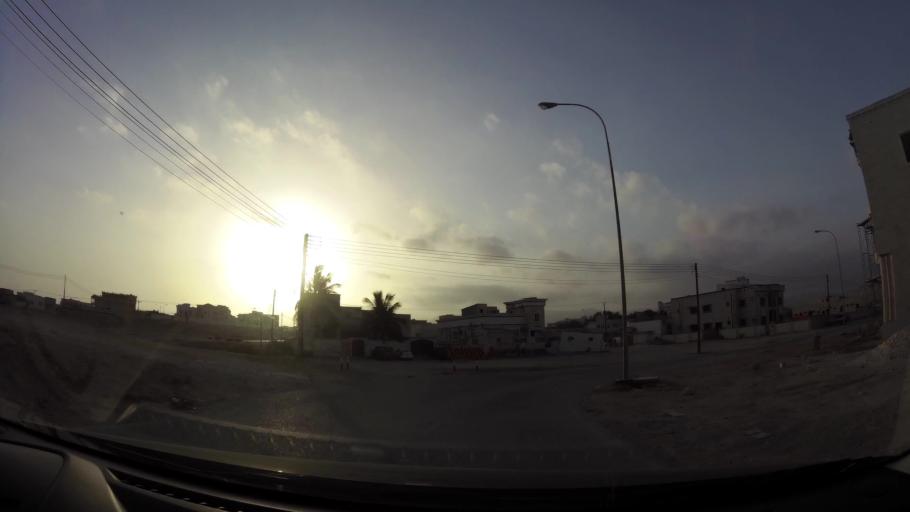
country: OM
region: Zufar
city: Salalah
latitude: 17.0006
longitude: 54.0325
